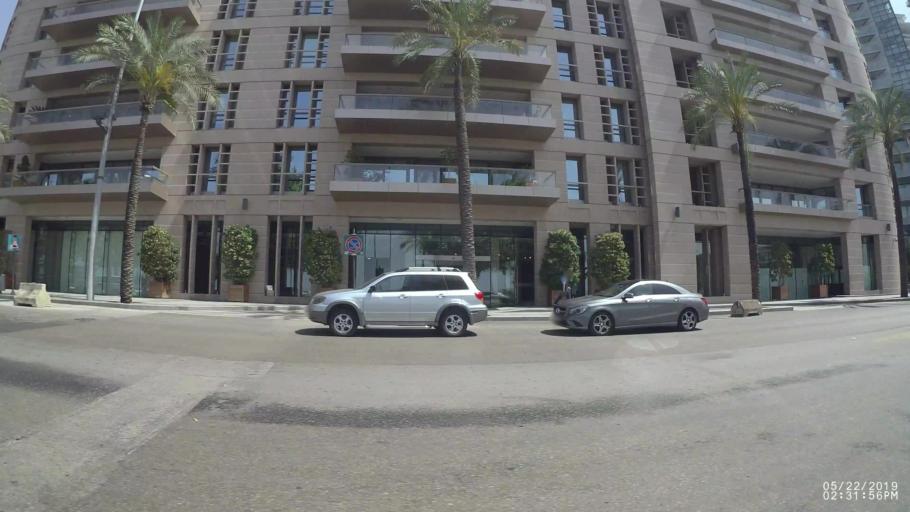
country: LB
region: Beyrouth
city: Beirut
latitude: 33.9011
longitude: 35.4977
